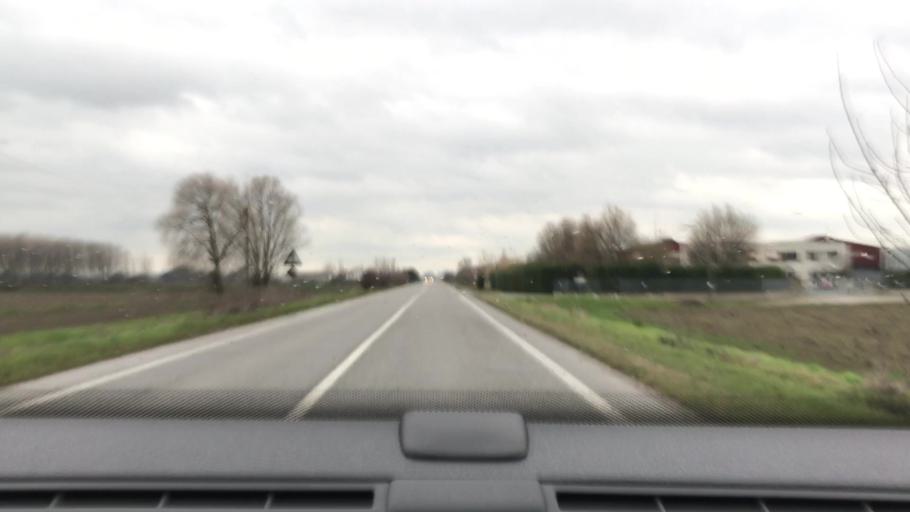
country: IT
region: Lombardy
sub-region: Provincia di Cremona
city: Torricella del Pizzo
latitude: 45.0328
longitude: 10.3041
